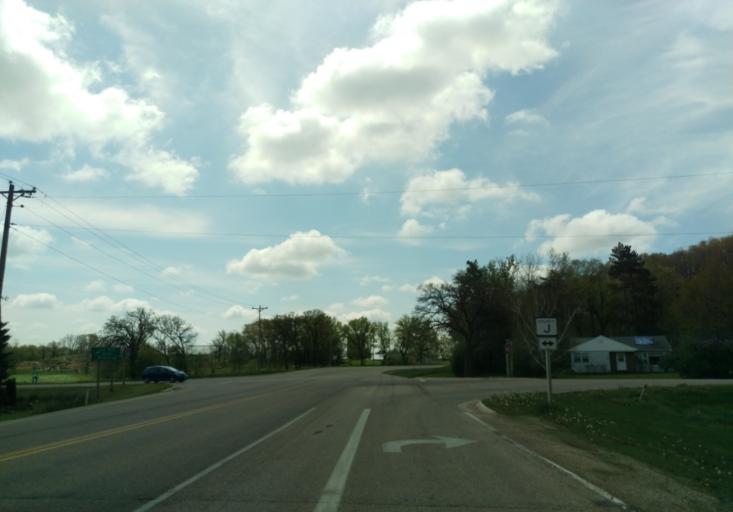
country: US
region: Wisconsin
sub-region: Dane County
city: Cross Plains
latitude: 43.0465
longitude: -89.6551
